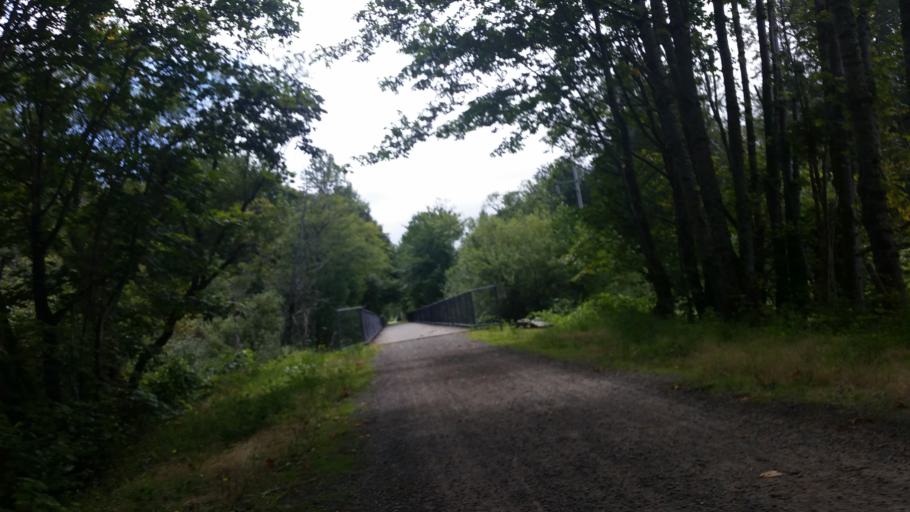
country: US
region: Washington
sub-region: King County
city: North Bend
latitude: 47.5042
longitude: -121.7881
